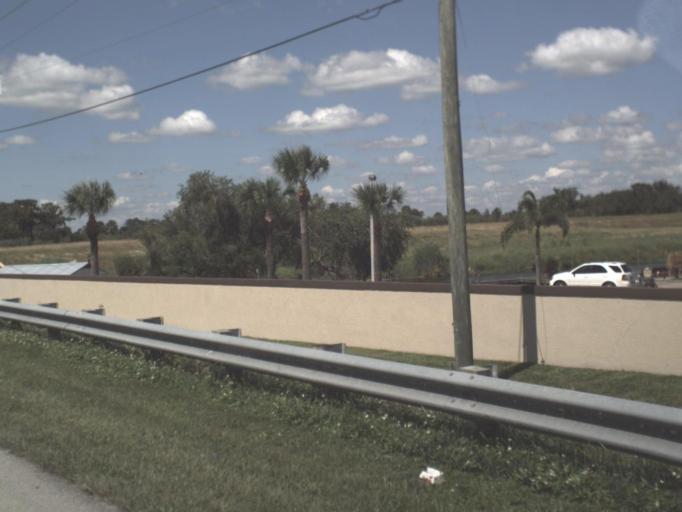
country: US
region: Florida
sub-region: Okeechobee County
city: Taylor Creek
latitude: 27.1928
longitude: -80.7596
